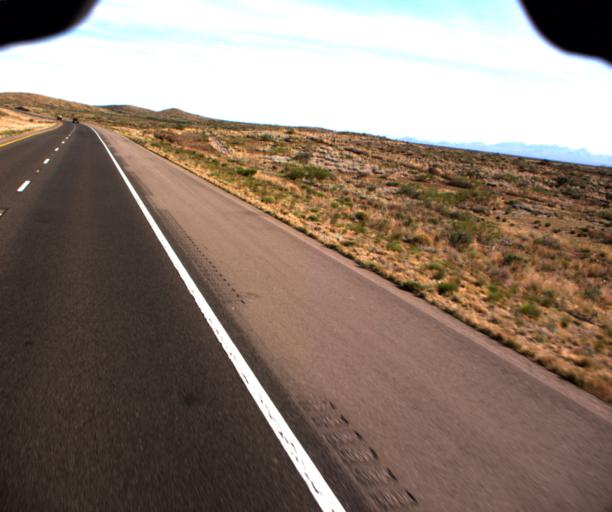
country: US
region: Arizona
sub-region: Cochise County
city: Willcox
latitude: 32.4433
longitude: -109.6635
